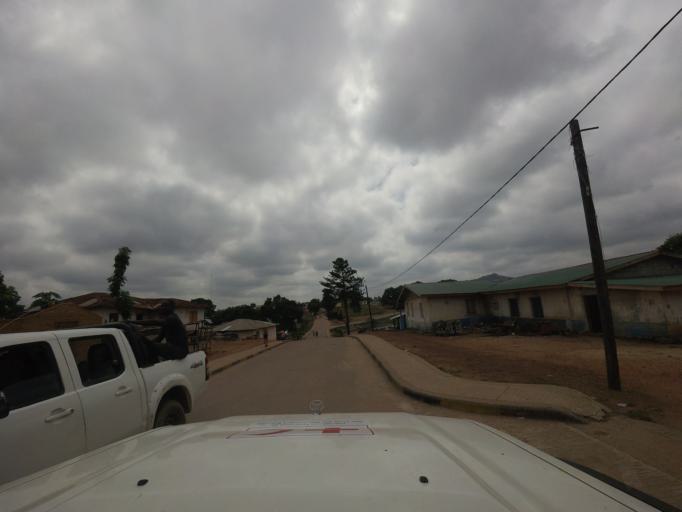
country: LR
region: Lofa
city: Voinjama
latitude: 8.4218
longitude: -9.7517
